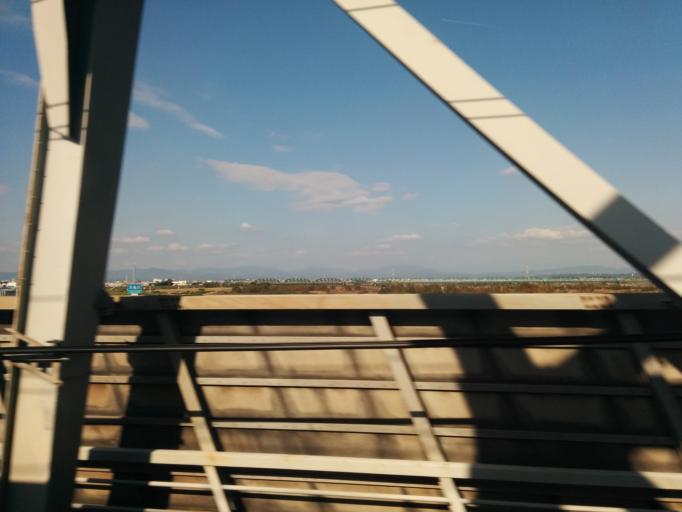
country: JP
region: Shizuoka
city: Iwata
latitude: 34.7068
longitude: 137.7960
